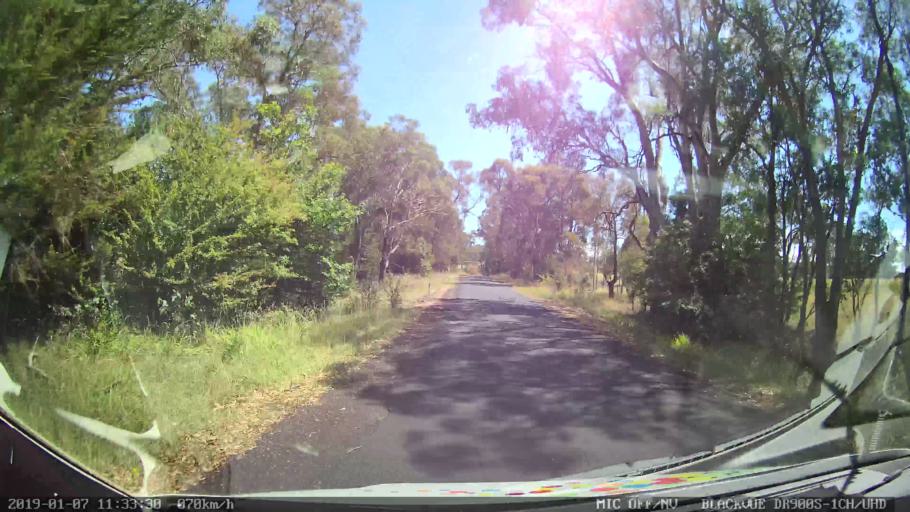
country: AU
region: New South Wales
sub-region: Armidale Dumaresq
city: Armidale
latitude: -30.3993
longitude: 151.5610
